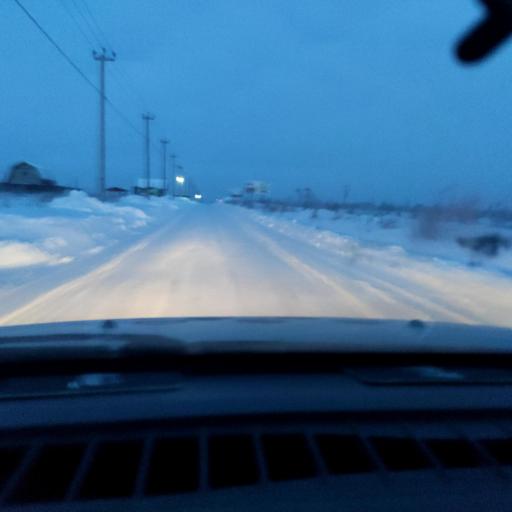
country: RU
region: Perm
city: Kultayevo
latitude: 57.8741
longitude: 55.9785
